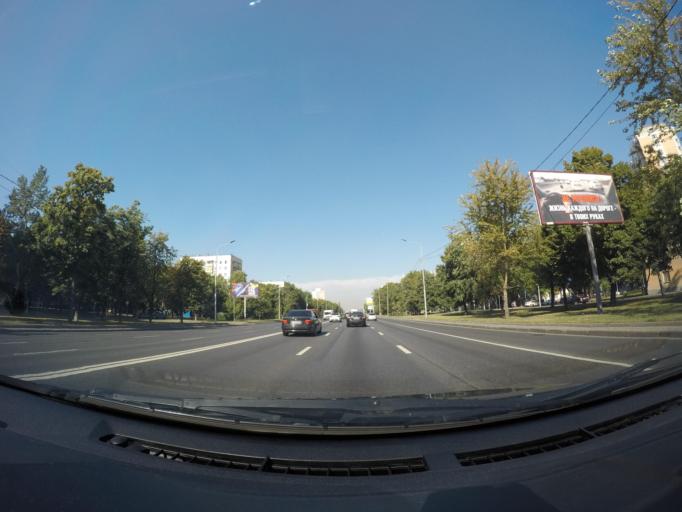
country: RU
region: Moscow
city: Novyye Kuz'minki
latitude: 55.7063
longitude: 37.7589
